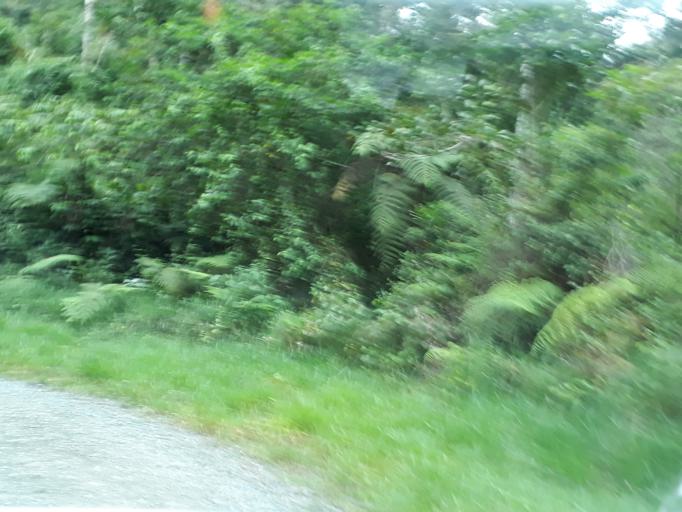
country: CO
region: Boyaca
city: Muzo
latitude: 5.3817
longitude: -74.0844
